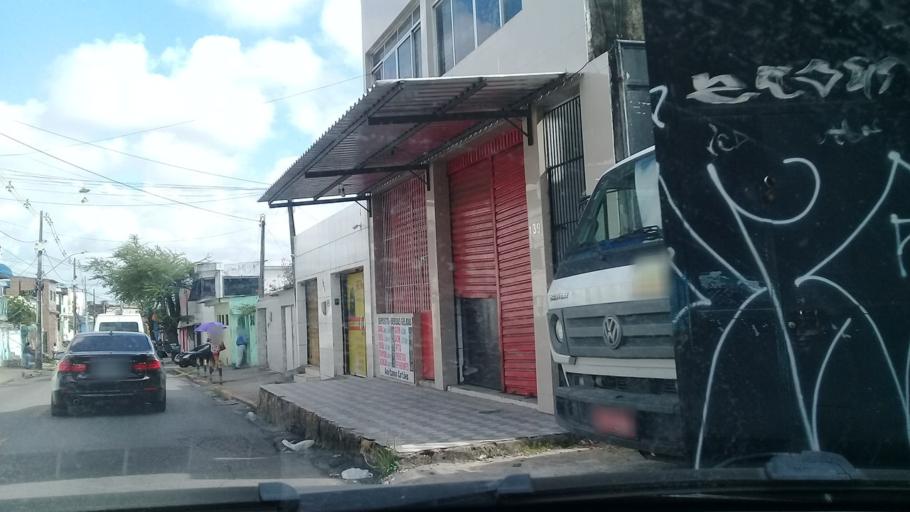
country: BR
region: Pernambuco
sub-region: Jaboatao Dos Guararapes
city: Jaboatao dos Guararapes
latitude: -8.1167
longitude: -34.9469
